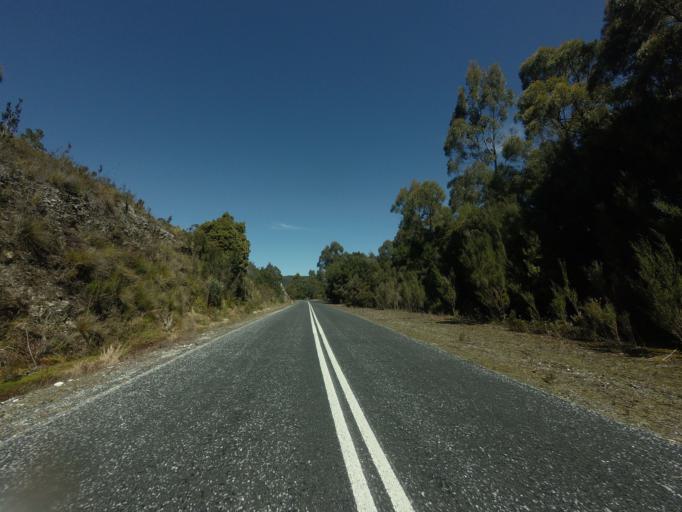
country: AU
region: Tasmania
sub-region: West Coast
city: Queenstown
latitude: -42.7955
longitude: 146.0864
